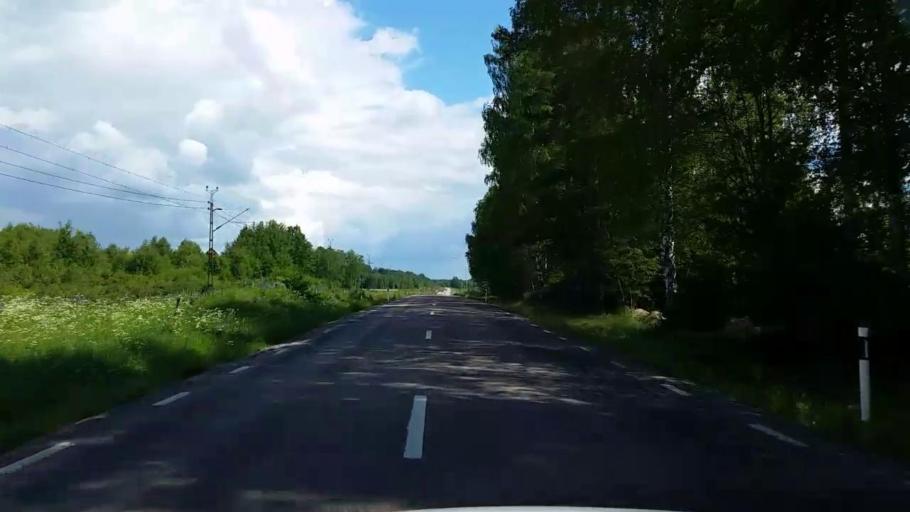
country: SE
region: Dalarna
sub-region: Avesta Kommun
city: Avesta
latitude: 60.1498
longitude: 16.2376
